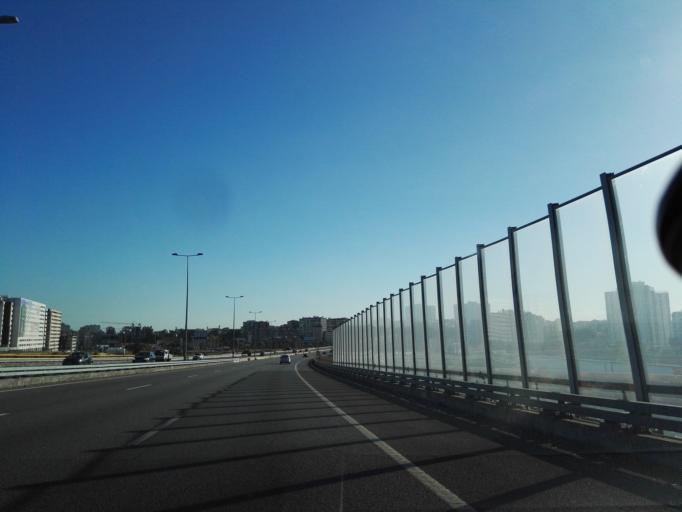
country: PT
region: Lisbon
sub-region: Odivelas
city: Olival do Basto
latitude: 38.7819
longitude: -9.1556
